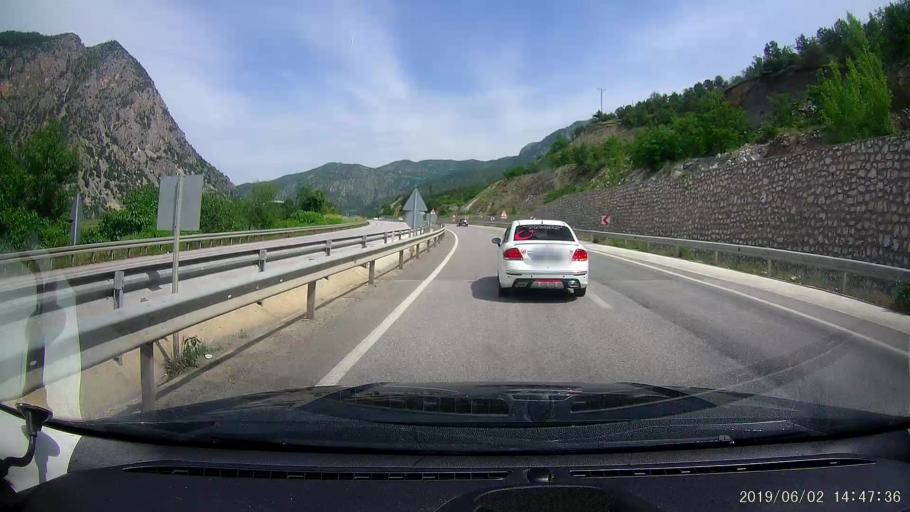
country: TR
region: Corum
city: Hacihamza
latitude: 41.0666
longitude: 34.4633
